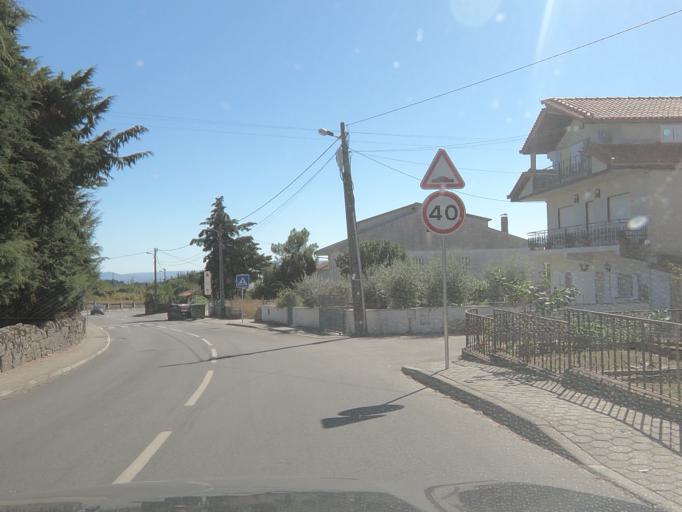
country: PT
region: Vila Real
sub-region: Valpacos
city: Valpacos
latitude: 41.6602
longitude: -7.3206
